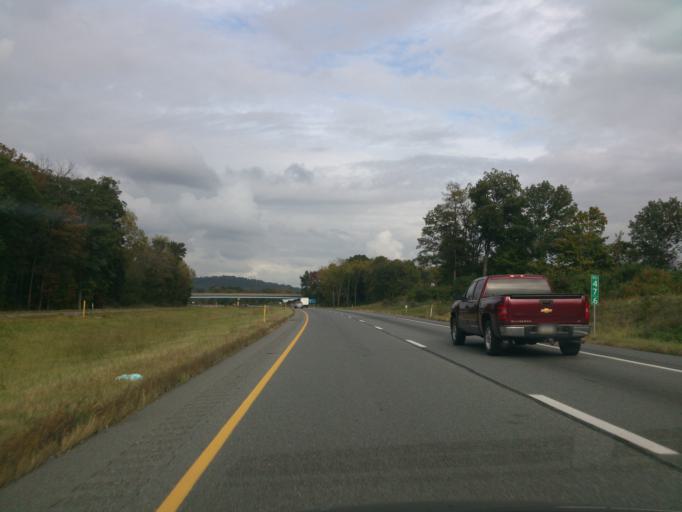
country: US
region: Pennsylvania
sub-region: Lancaster County
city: Adamstown
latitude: 40.2258
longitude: -76.0588
